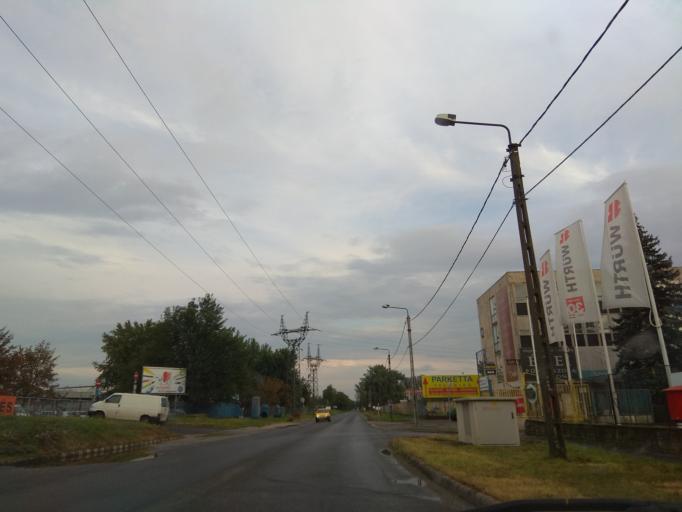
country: HU
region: Borsod-Abauj-Zemplen
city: Miskolc
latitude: 48.1064
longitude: 20.8205
